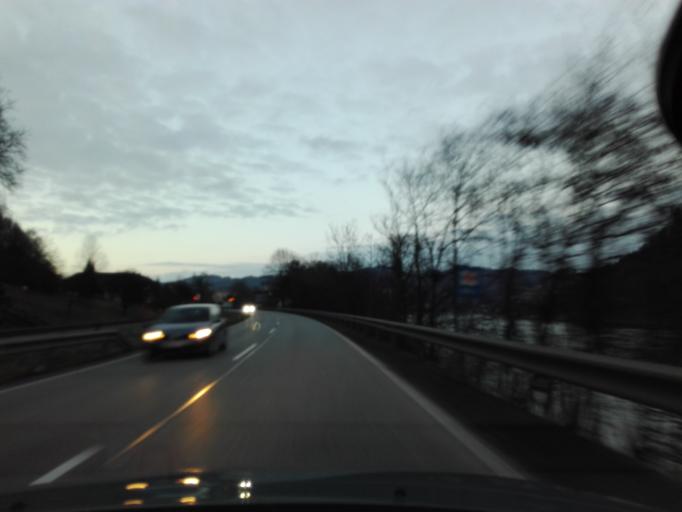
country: AT
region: Upper Austria
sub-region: Politischer Bezirk Perg
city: Bad Kreuzen
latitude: 48.2151
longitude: 14.8557
